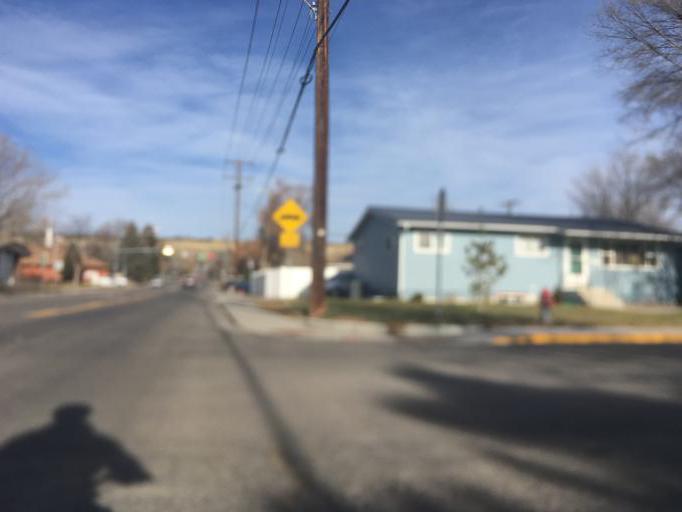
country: US
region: Montana
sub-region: Yellowstone County
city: Billings
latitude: 45.7890
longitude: -108.5590
